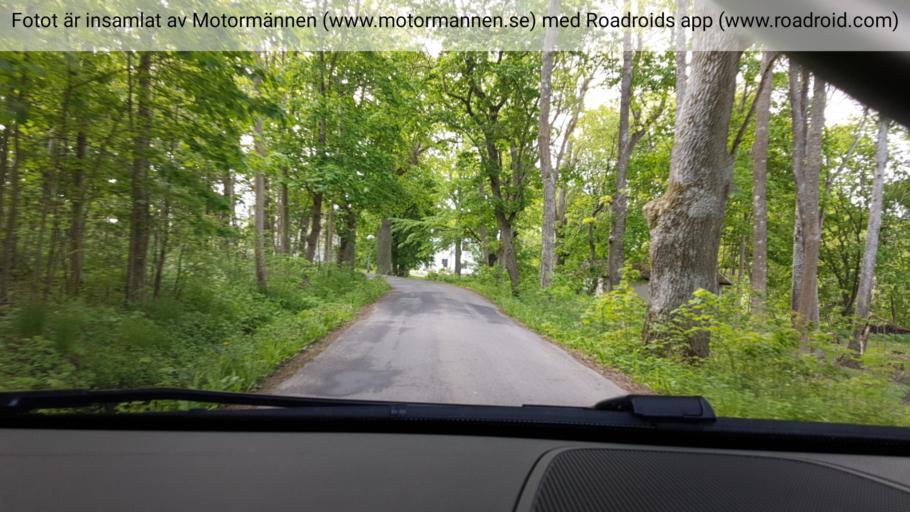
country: SE
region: Stockholm
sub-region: Haninge Kommun
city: Jordbro
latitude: 59.0085
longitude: 18.1208
